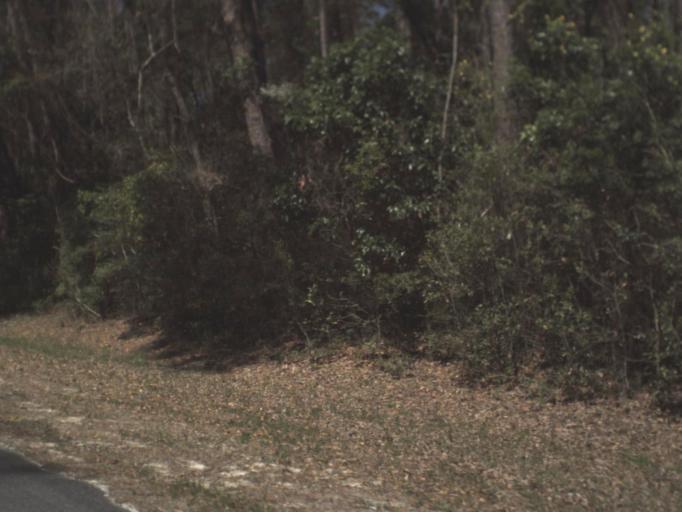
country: US
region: Florida
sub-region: Leon County
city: Woodville
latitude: 30.2413
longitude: -84.2752
